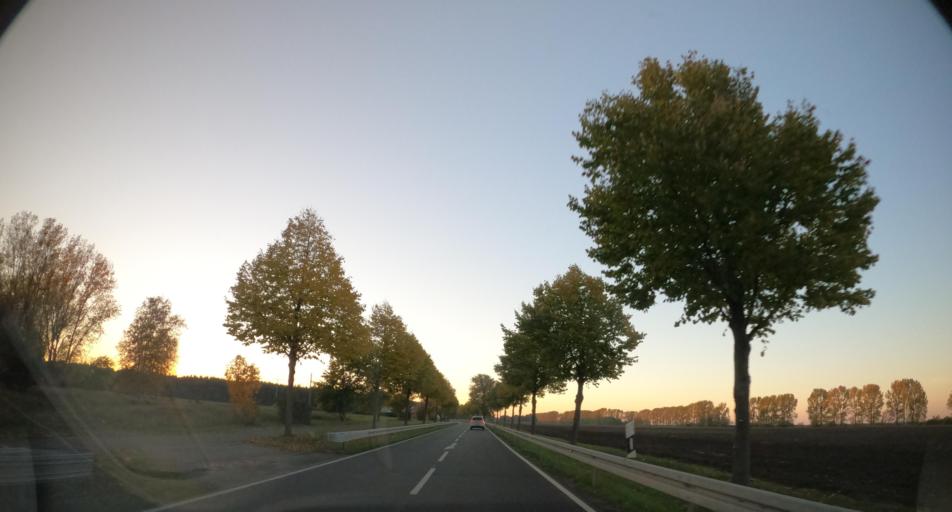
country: DE
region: Mecklenburg-Vorpommern
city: Ueckermunde
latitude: 53.7622
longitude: 14.0032
